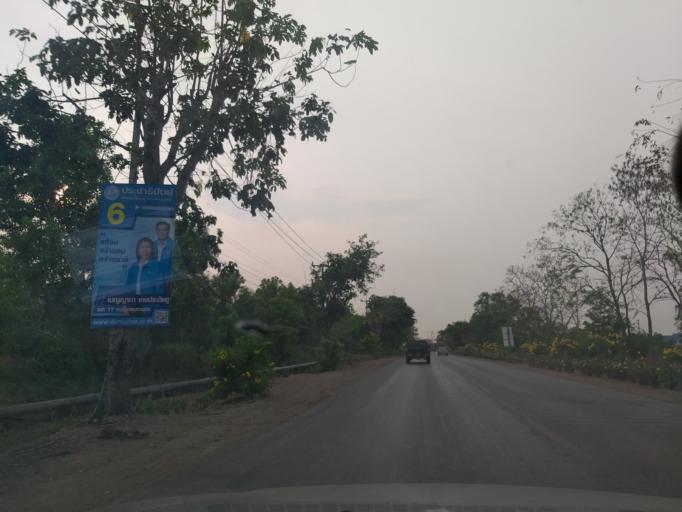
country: TH
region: Bangkok
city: Nong Chok
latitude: 13.8374
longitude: 100.9043
